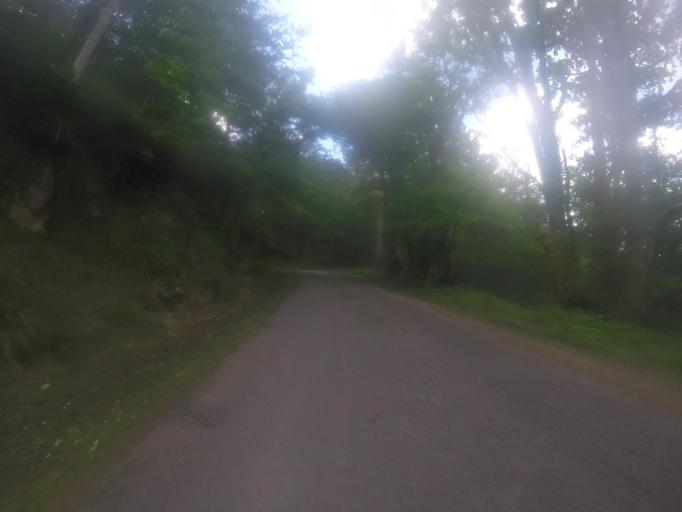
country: ES
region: Navarre
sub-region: Provincia de Navarra
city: Arantza
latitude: 43.2251
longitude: -1.8010
